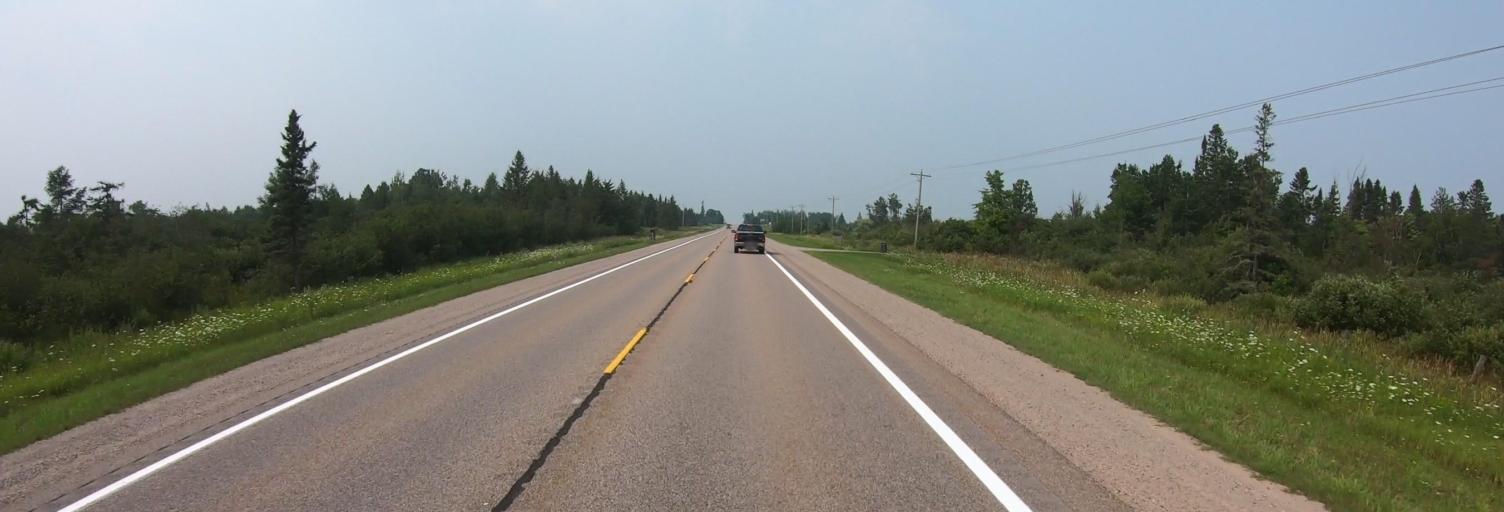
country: US
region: Michigan
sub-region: Chippewa County
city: Sault Ste. Marie
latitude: 46.3112
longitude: -84.3638
